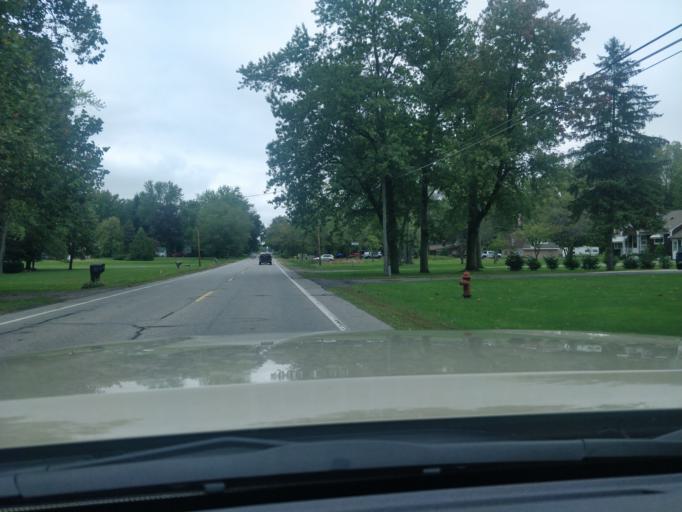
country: US
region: Michigan
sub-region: Wayne County
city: Romulus
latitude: 42.1705
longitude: -83.4031
